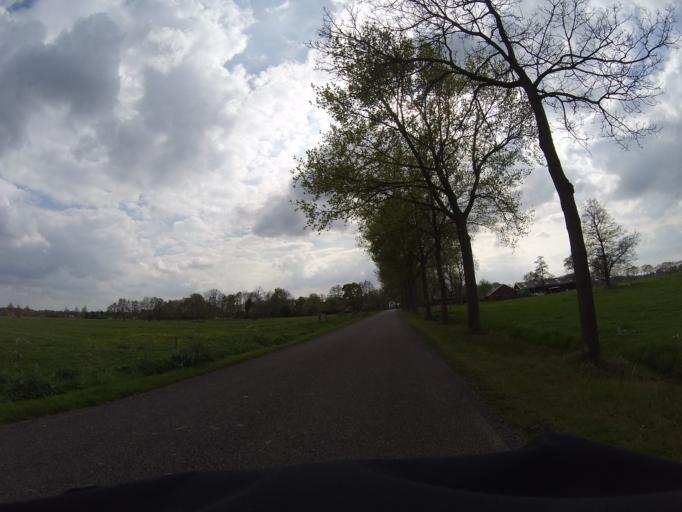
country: NL
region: Gelderland
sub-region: Gemeente Oldebroek
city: Oldebroek
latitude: 52.4527
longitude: 5.9465
